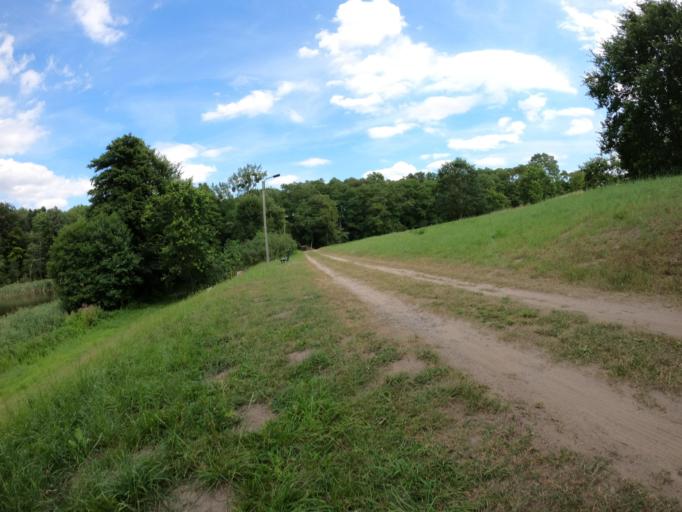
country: DE
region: Mecklenburg-Vorpommern
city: Woldegk
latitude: 53.3554
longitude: 13.5921
